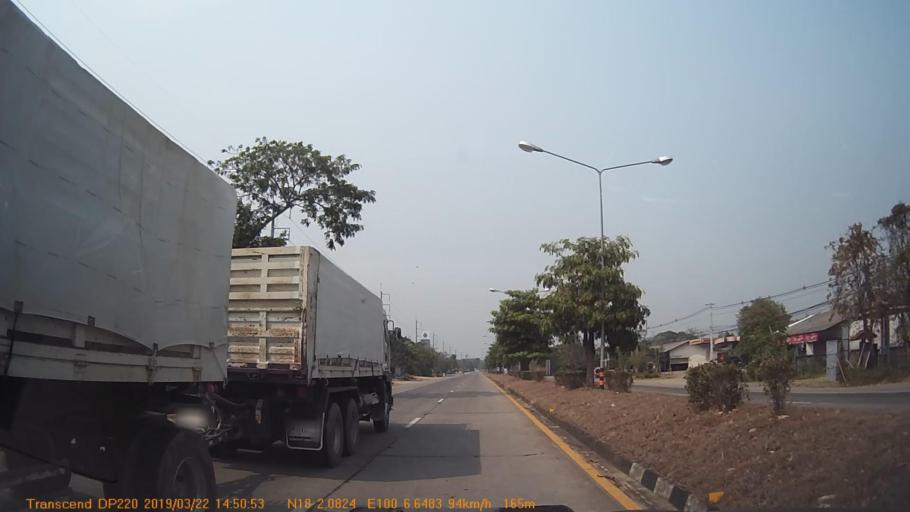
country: TH
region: Phrae
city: Sung Men
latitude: 18.0350
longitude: 100.1108
